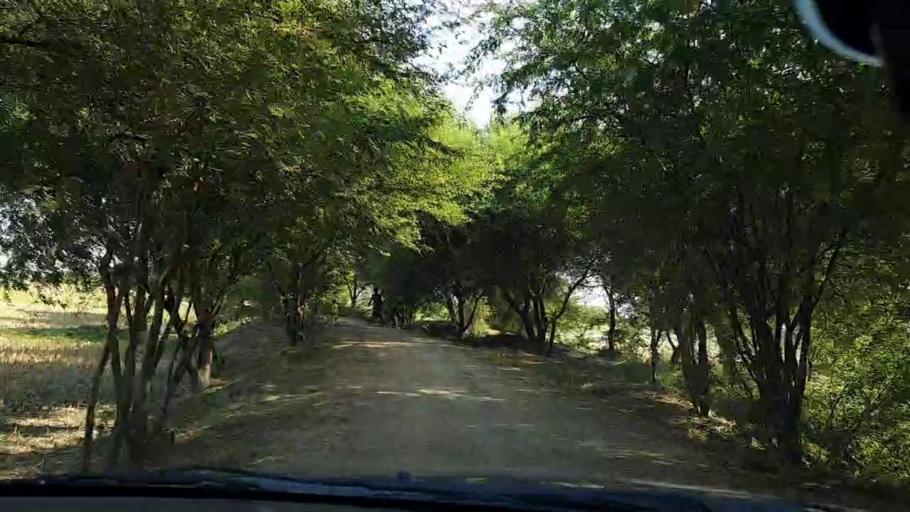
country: PK
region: Sindh
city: Mirpur Batoro
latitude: 24.6297
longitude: 68.2657
